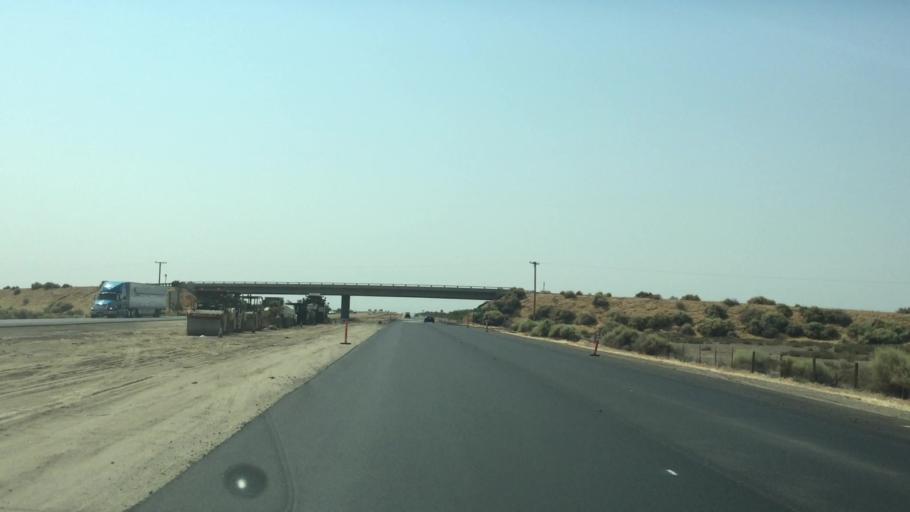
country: US
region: California
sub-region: Kern County
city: Lost Hills
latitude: 35.7911
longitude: -119.7838
